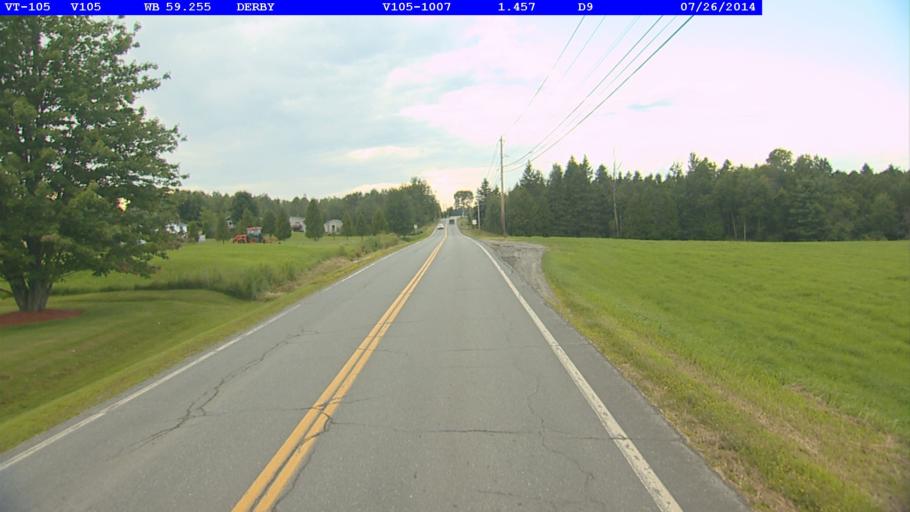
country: US
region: Vermont
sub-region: Orleans County
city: Newport
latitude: 44.9371
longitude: -72.1241
